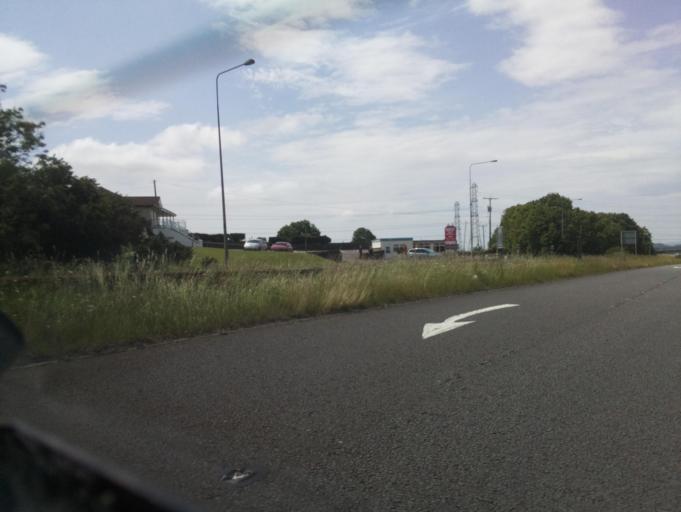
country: GB
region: Wales
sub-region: Vale of Glamorgan
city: Cowbridge
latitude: 51.4586
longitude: -3.4204
